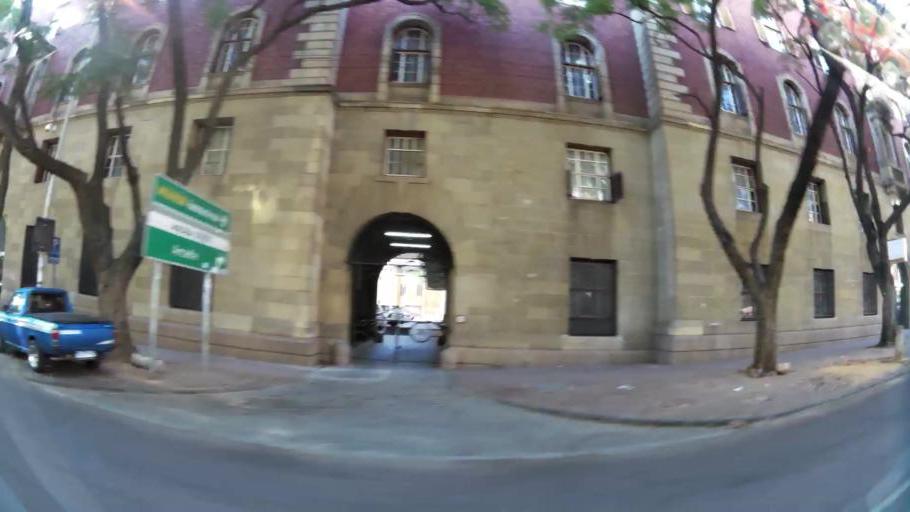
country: ZA
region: Gauteng
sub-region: City of Tshwane Metropolitan Municipality
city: Pretoria
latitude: -25.7459
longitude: 28.1857
